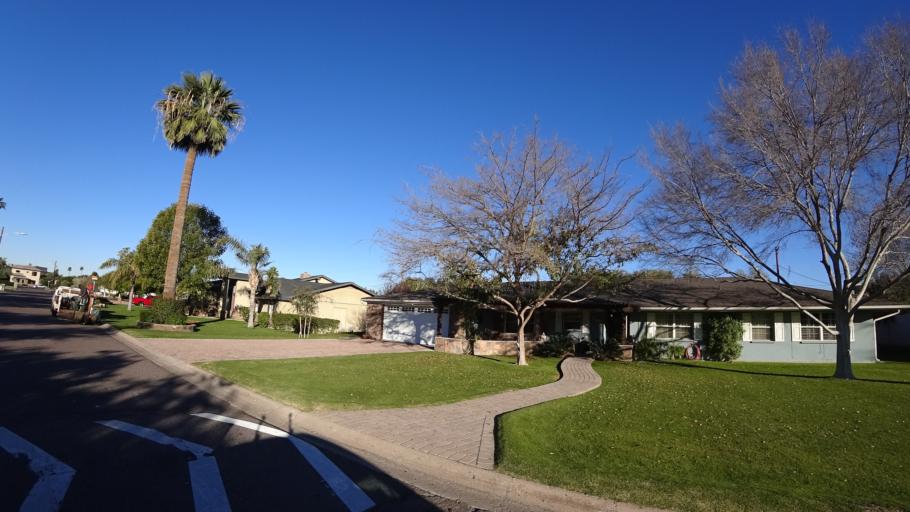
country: US
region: Arizona
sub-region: Maricopa County
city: Paradise Valley
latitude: 33.5109
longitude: -112.0066
